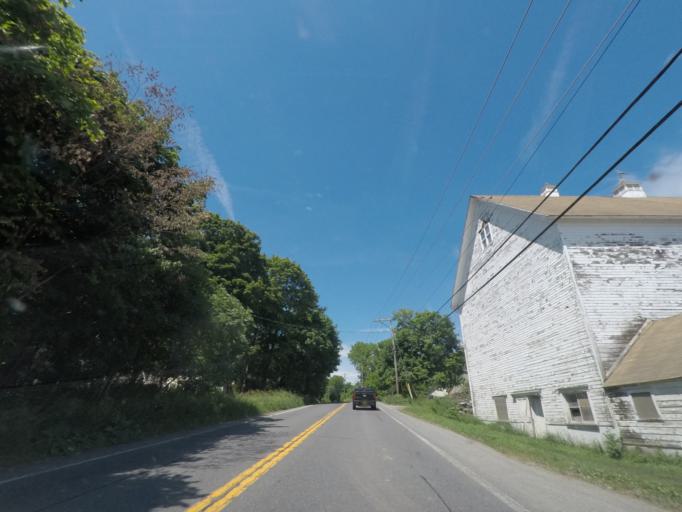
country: US
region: Massachusetts
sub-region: Berkshire County
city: Great Barrington
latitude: 42.2106
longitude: -73.5080
